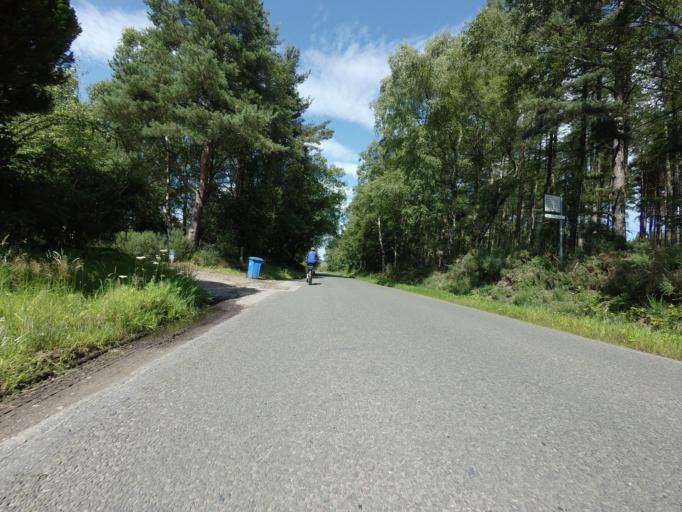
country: GB
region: Scotland
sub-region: Highland
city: Conon Bridge
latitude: 57.5372
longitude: -4.3264
